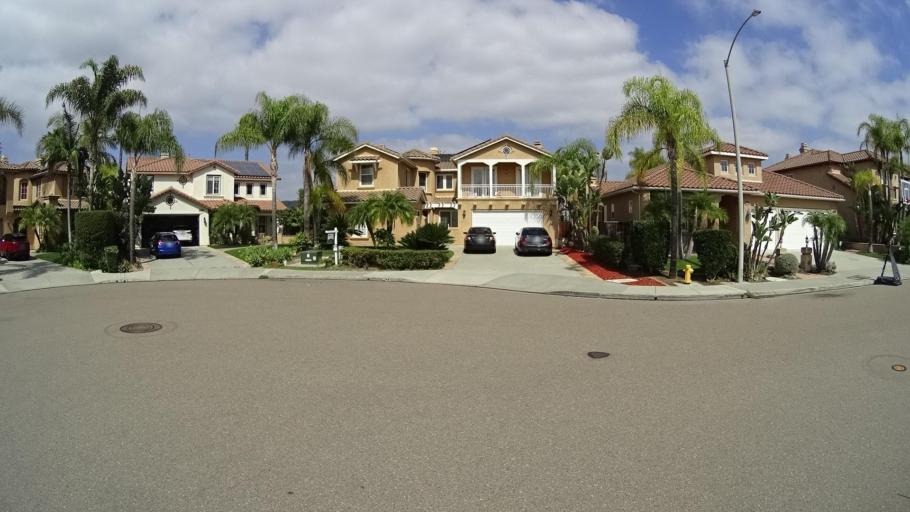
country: US
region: California
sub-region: San Diego County
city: Fairbanks Ranch
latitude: 33.0137
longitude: -117.1084
